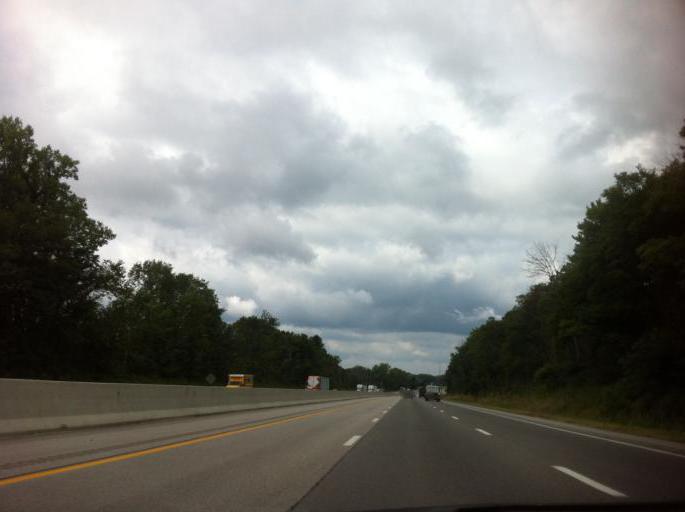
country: US
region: Ohio
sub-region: Summit County
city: Hudson
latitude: 41.2552
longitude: -81.4660
